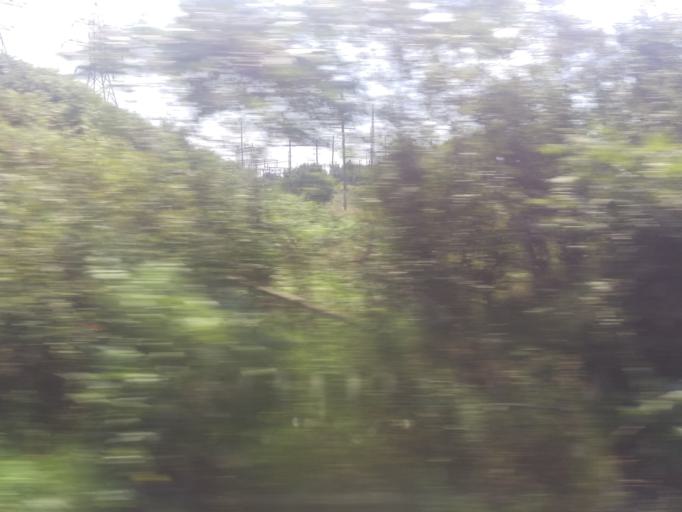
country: CA
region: Ontario
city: Kingston
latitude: 44.2609
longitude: -76.4984
